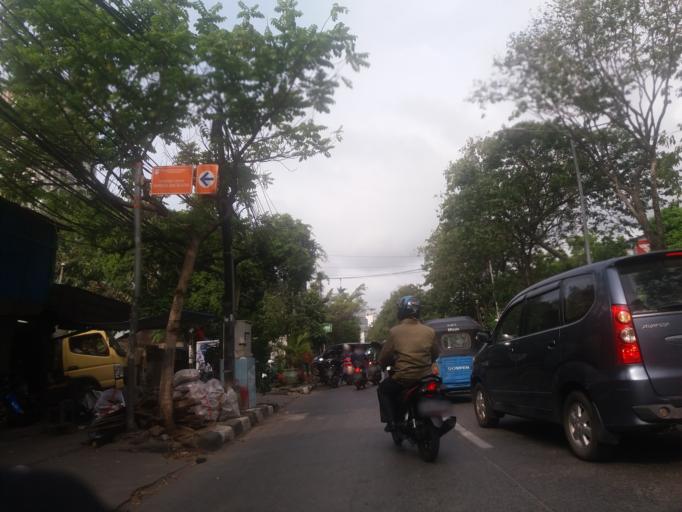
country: ID
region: Jakarta Raya
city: Jakarta
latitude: -6.1407
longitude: 106.8251
